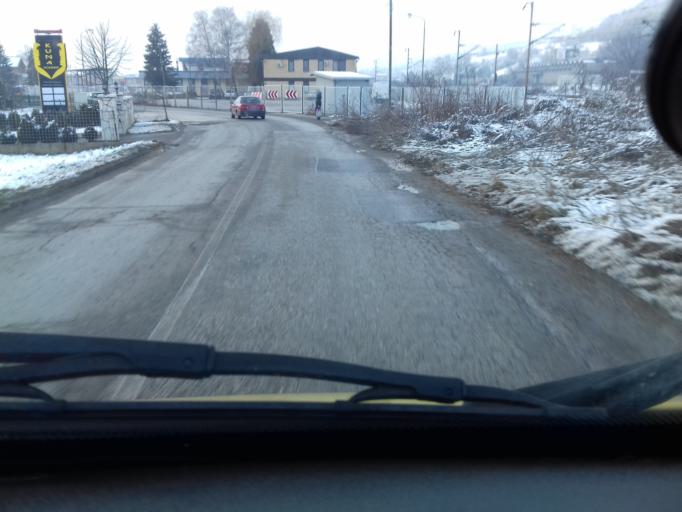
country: BA
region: Federation of Bosnia and Herzegovina
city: Visoko
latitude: 43.9986
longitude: 18.1803
